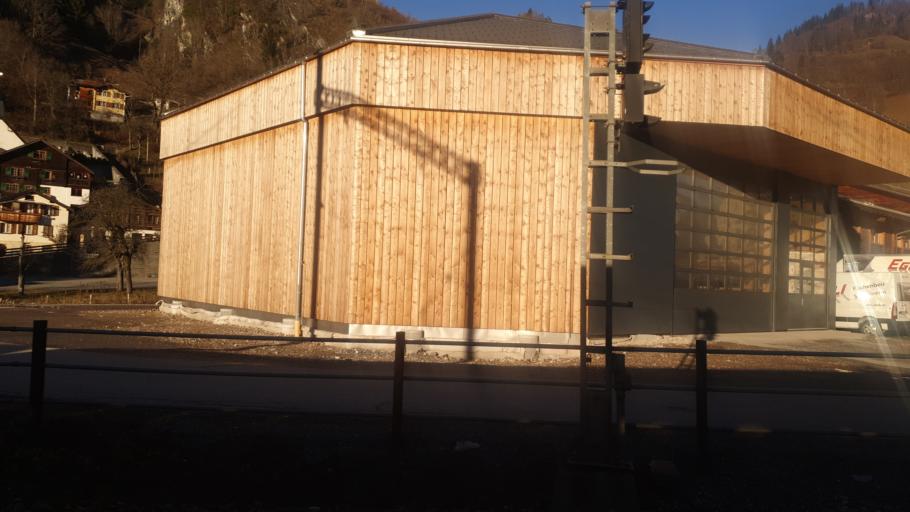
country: CH
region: Grisons
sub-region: Praettigau/Davos District
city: Grusch
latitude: 46.9810
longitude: 9.6446
